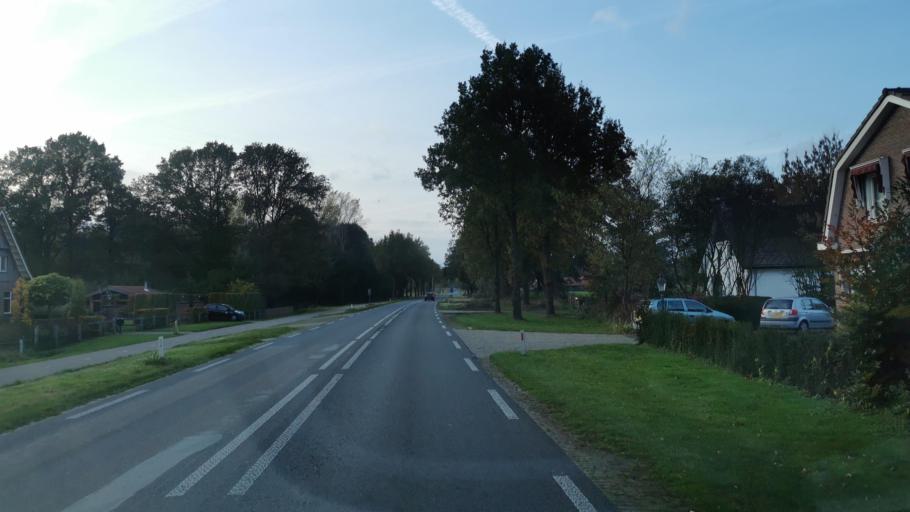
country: NL
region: Overijssel
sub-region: Gemeente Oldenzaal
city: Oldenzaal
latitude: 52.2871
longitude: 6.9474
